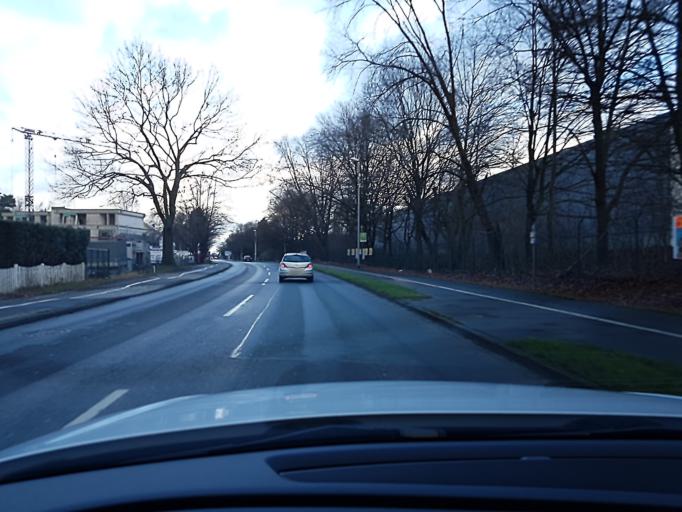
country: DE
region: North Rhine-Westphalia
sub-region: Regierungsbezirk Dusseldorf
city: Muelheim (Ruhr)
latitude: 51.3910
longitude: 6.8694
